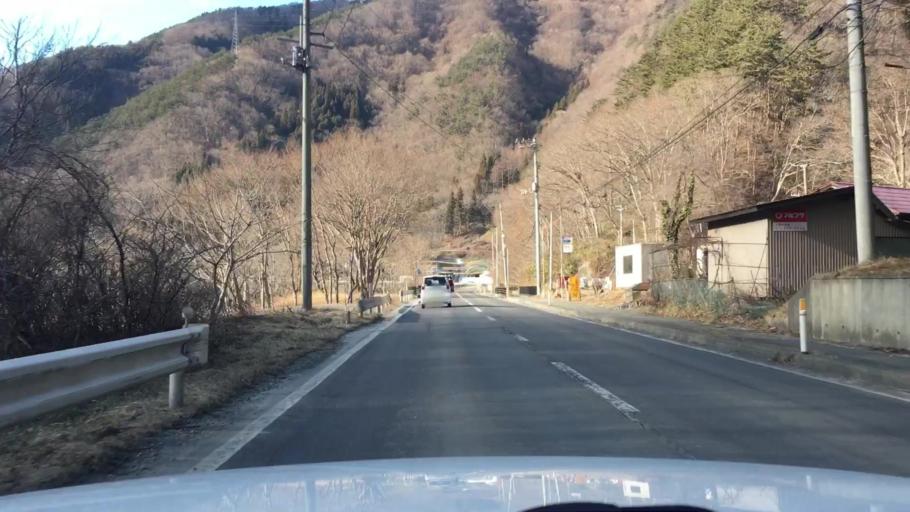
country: JP
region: Iwate
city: Miyako
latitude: 39.6028
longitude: 141.7004
